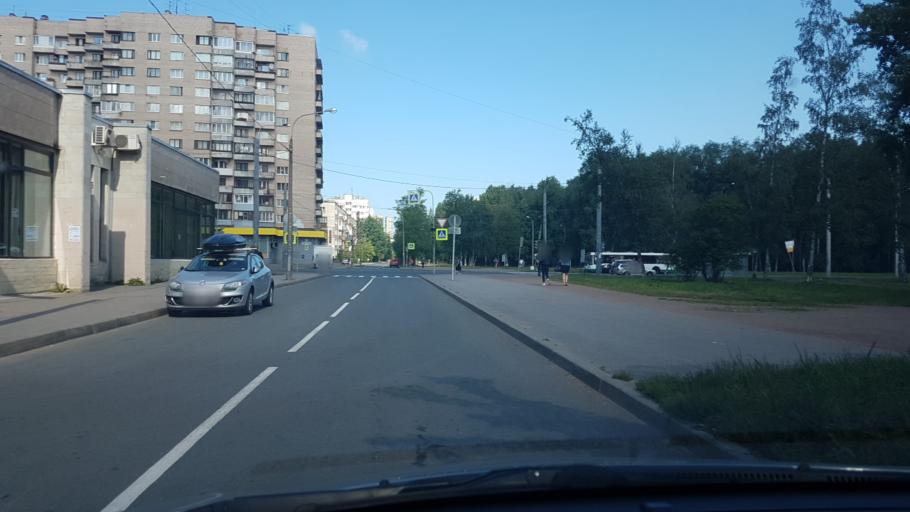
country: RU
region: St.-Petersburg
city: Dachnoye
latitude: 59.8344
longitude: 30.2234
